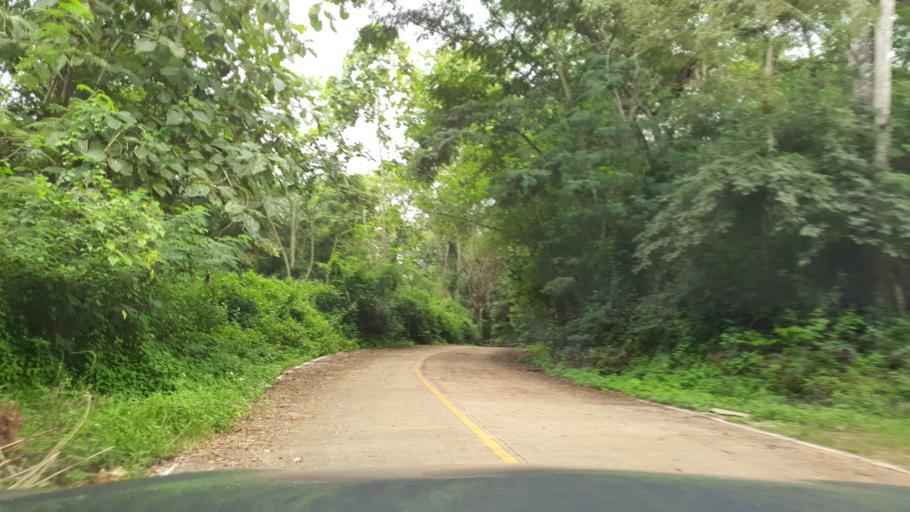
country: TH
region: Chiang Mai
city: San Sai
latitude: 18.9376
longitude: 98.9173
